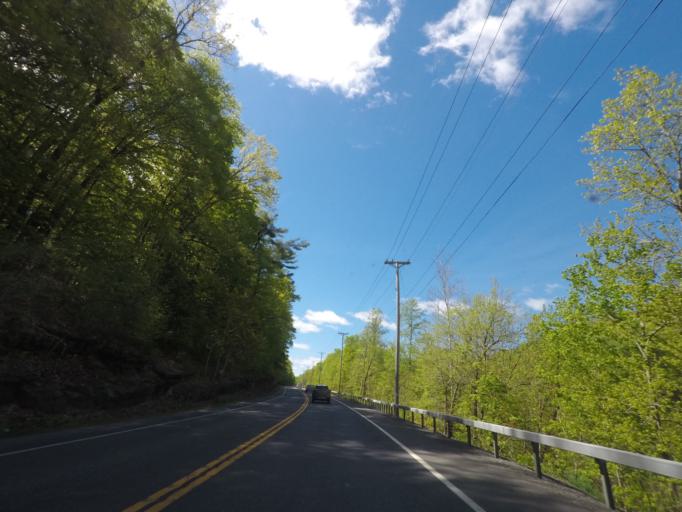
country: US
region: New York
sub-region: Ulster County
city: Glasco
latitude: 42.0264
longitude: -73.9767
